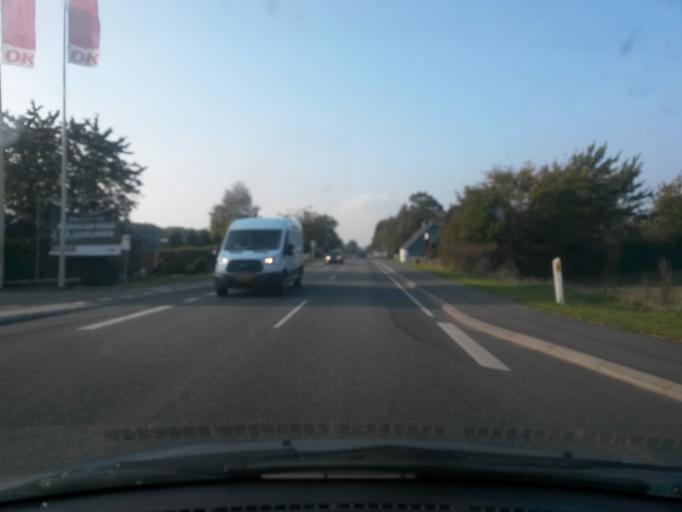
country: DK
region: Central Jutland
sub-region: Syddjurs Kommune
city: Hornslet
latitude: 56.3573
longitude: 10.3404
